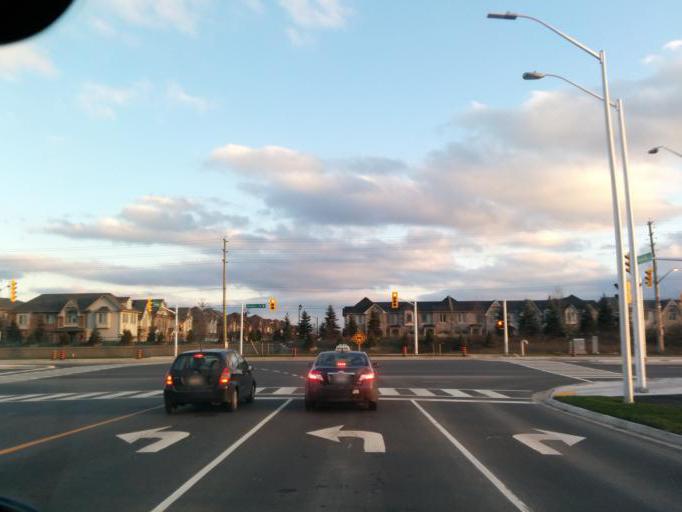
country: CA
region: Ontario
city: Oakville
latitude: 43.4477
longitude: -79.7645
